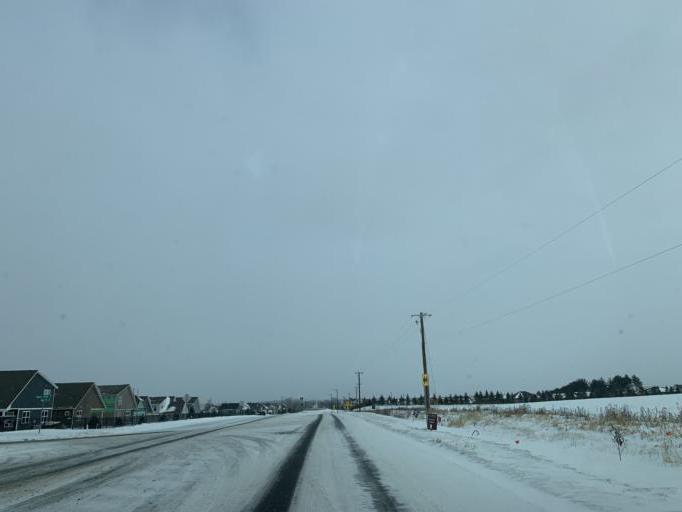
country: US
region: Minnesota
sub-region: Washington County
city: Cottage Grove
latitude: 44.8764
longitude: -92.9269
